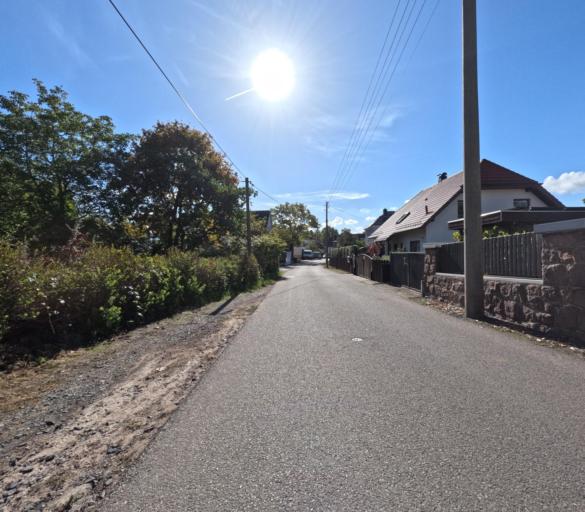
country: DE
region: Saxony
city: Radebeul
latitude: 51.1210
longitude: 13.6430
